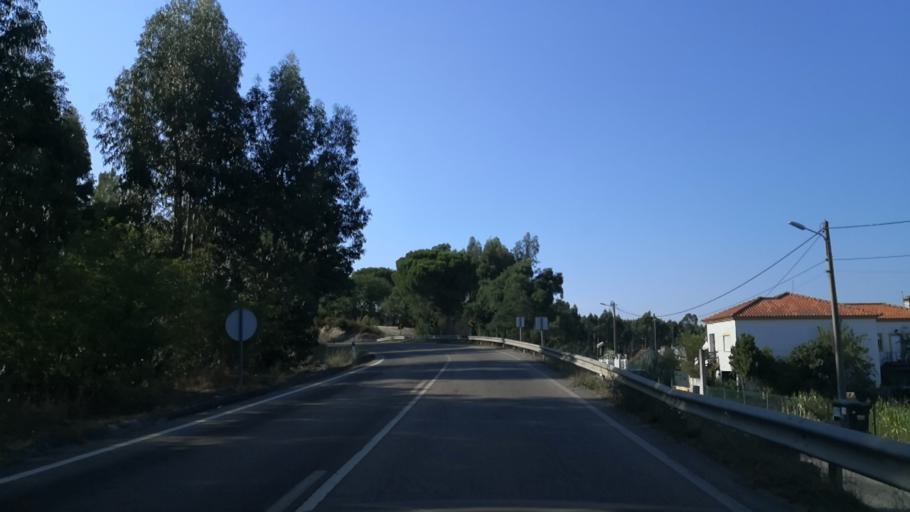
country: PT
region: Santarem
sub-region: Coruche
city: Coruche
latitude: 38.9699
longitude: -8.5366
